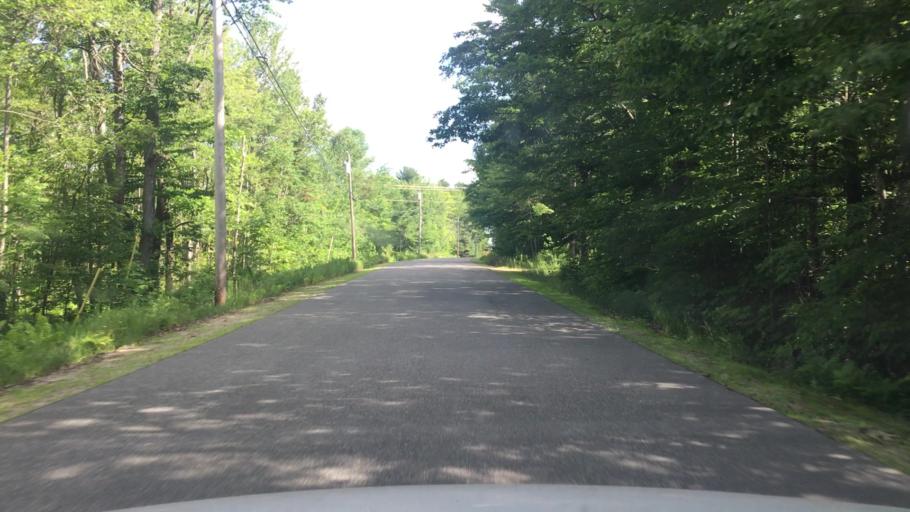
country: US
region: Maine
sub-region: Franklin County
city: Wilton
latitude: 44.6365
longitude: -70.1990
